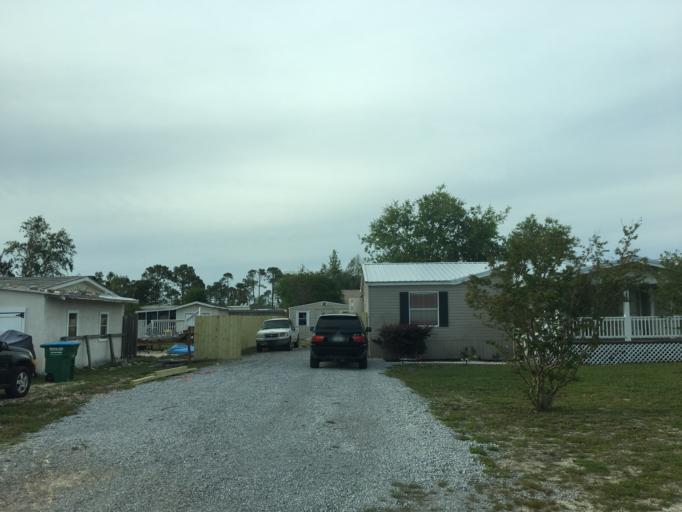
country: US
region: Florida
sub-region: Bay County
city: Upper Grand Lagoon
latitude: 30.1691
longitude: -85.7701
